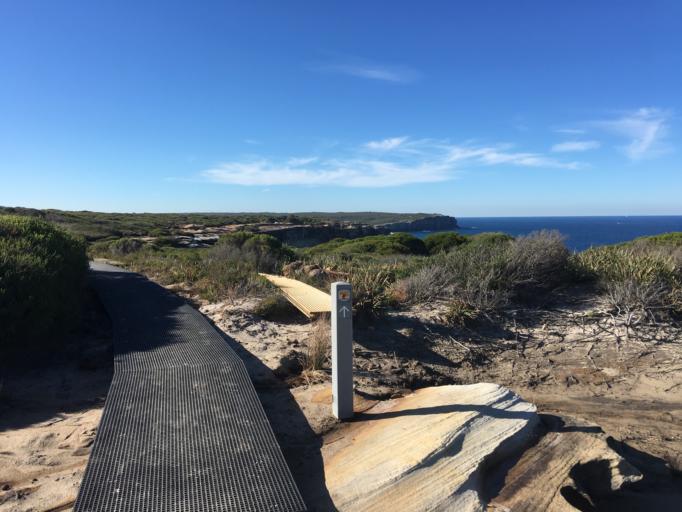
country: AU
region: New South Wales
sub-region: Sutherland Shire
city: Bundeena
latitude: -34.1288
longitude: 151.1310
